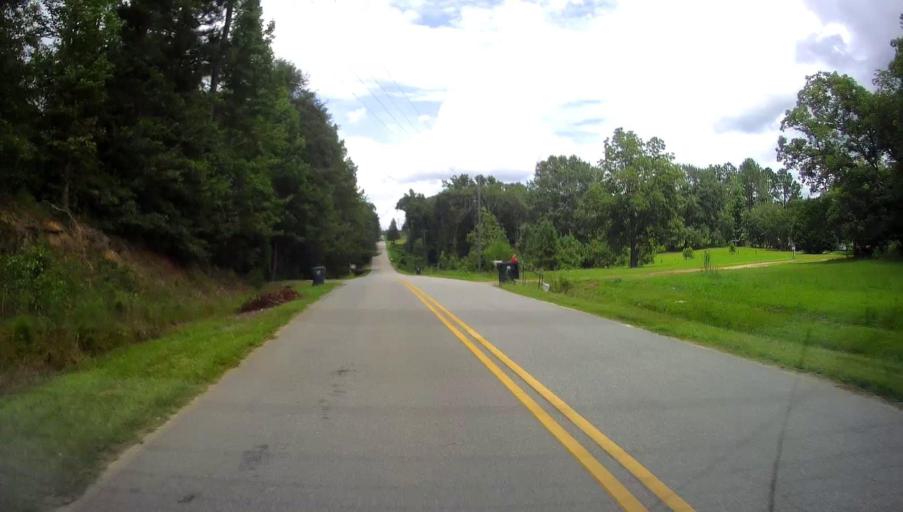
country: US
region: Georgia
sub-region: Houston County
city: Perry
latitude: 32.5506
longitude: -83.7533
